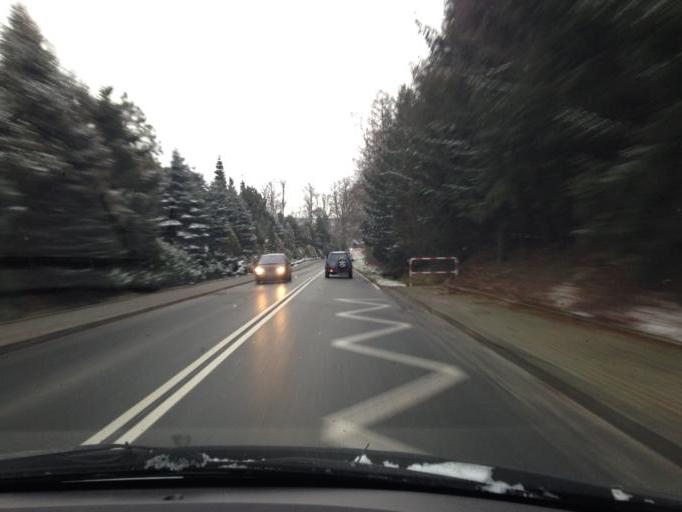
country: PL
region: Lesser Poland Voivodeship
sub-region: Powiat tarnowski
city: Gromnik
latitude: 49.8393
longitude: 20.9547
